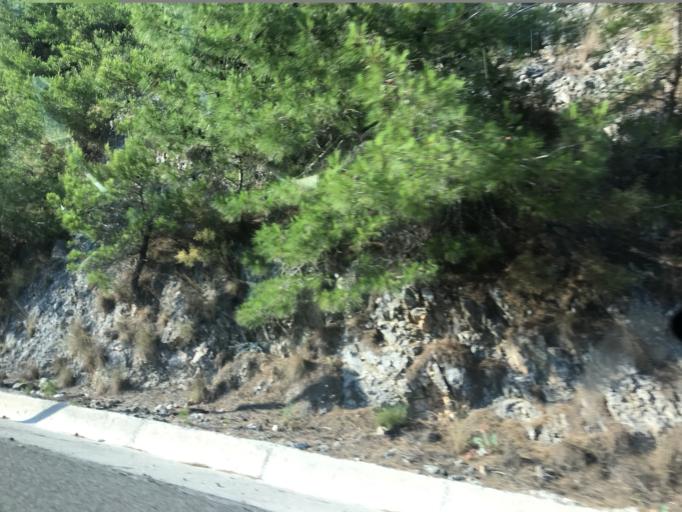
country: TR
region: Mugla
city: Ula
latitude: 37.0612
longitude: 28.3488
